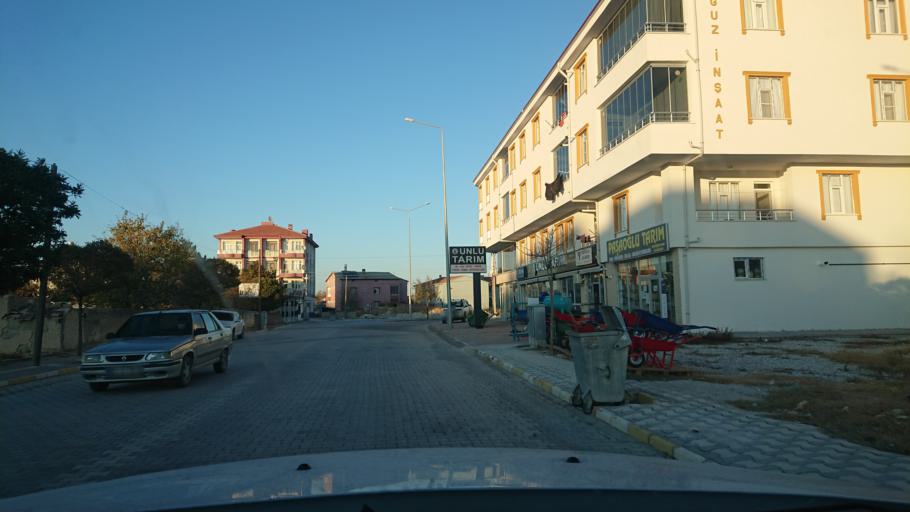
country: TR
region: Aksaray
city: Eskil
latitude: 38.4011
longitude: 33.4069
